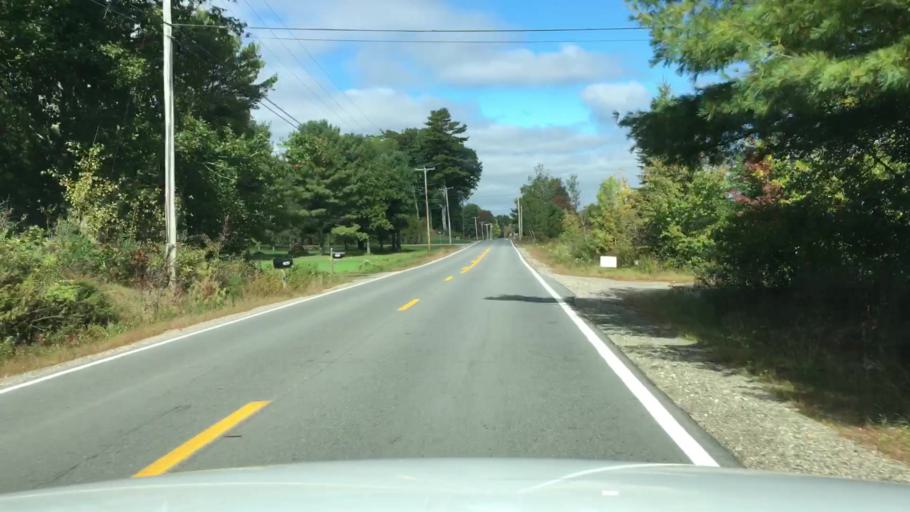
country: US
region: Maine
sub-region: Sagadahoc County
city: North Bath
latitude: 43.9955
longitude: -69.8901
